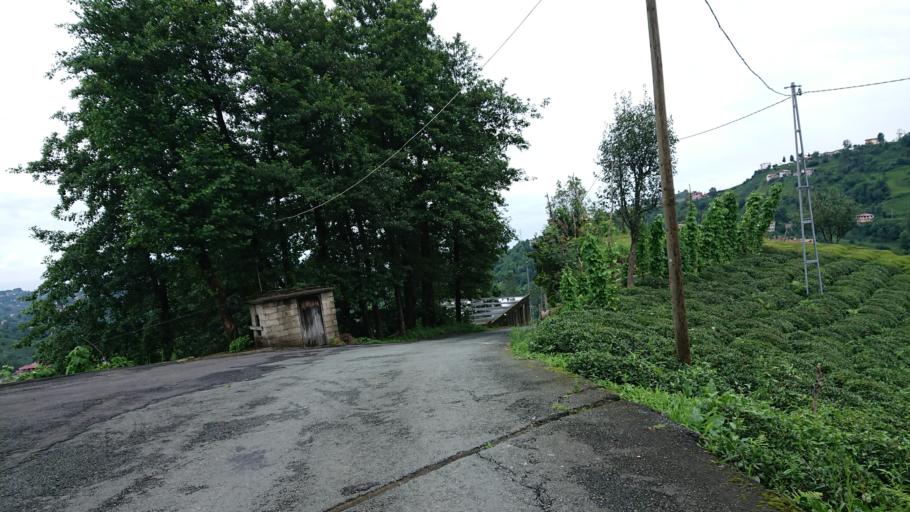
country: TR
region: Rize
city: Rize
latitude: 40.9849
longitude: 40.4852
